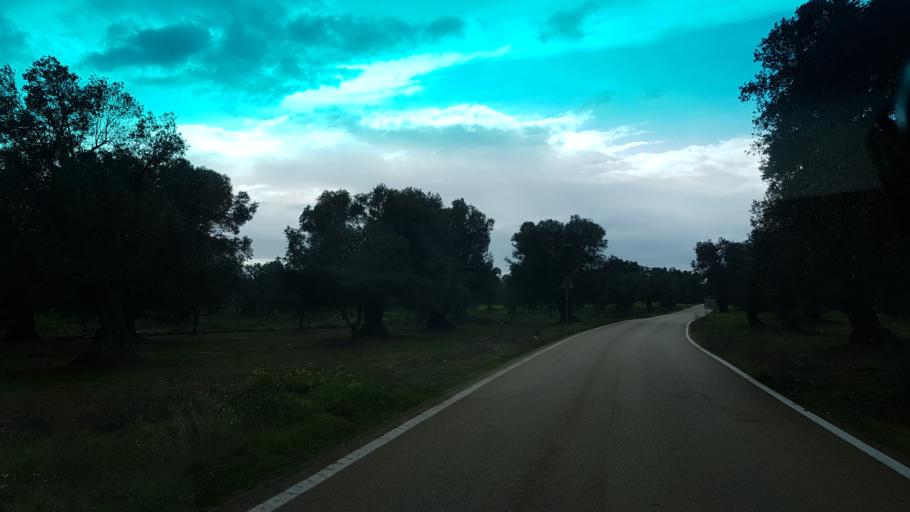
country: IT
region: Apulia
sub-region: Provincia di Brindisi
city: San Vito dei Normanni
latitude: 40.7079
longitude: 17.7660
